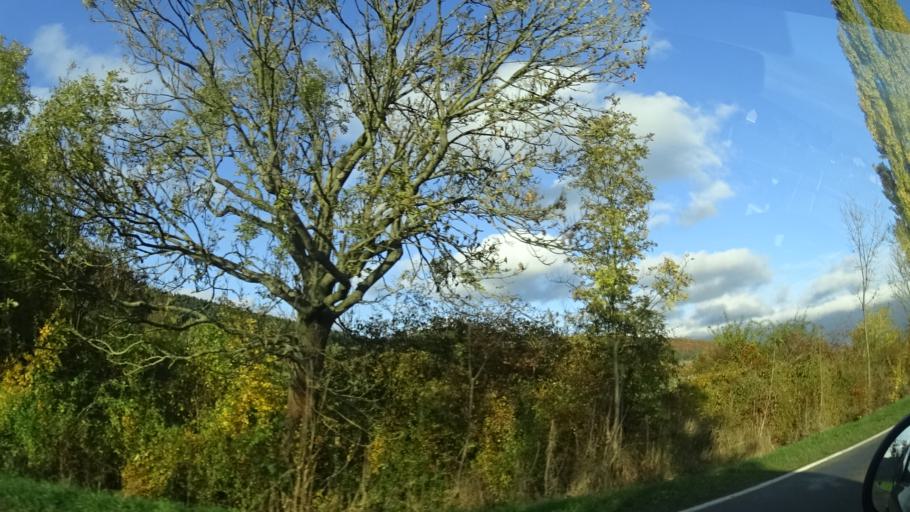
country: DE
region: Thuringia
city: Hohenfelden
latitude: 50.8815
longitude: 11.1549
